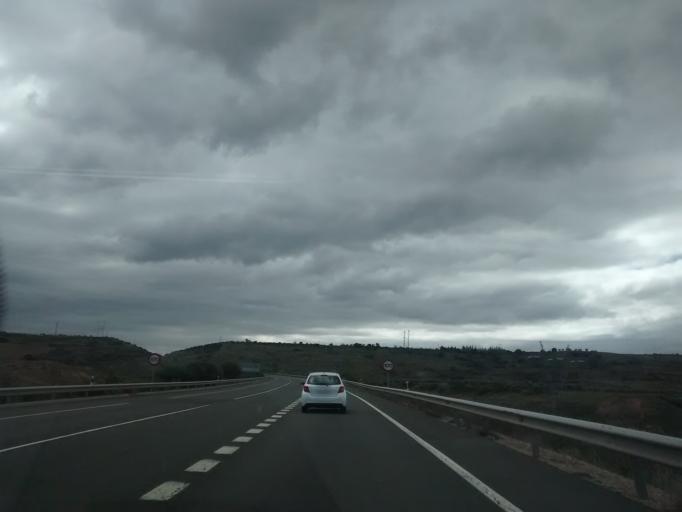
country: ES
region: La Rioja
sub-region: Provincia de La Rioja
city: Ausejo
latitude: 42.3404
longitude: -2.1752
